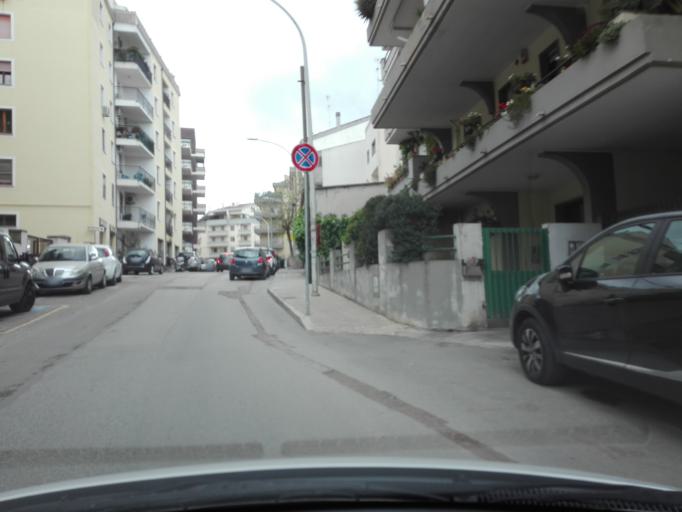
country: IT
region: Sardinia
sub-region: Provincia di Sassari
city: Sassari
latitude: 40.7285
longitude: 8.5783
